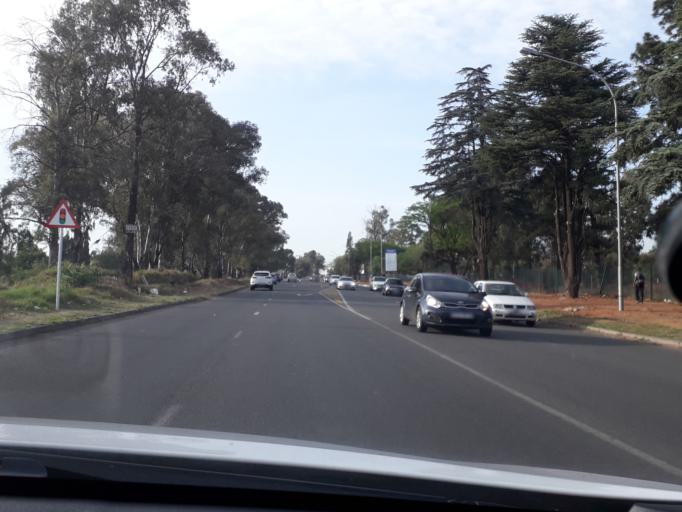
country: ZA
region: Gauteng
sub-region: City of Johannesburg Metropolitan Municipality
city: Modderfontein
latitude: -26.1455
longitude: 28.1238
